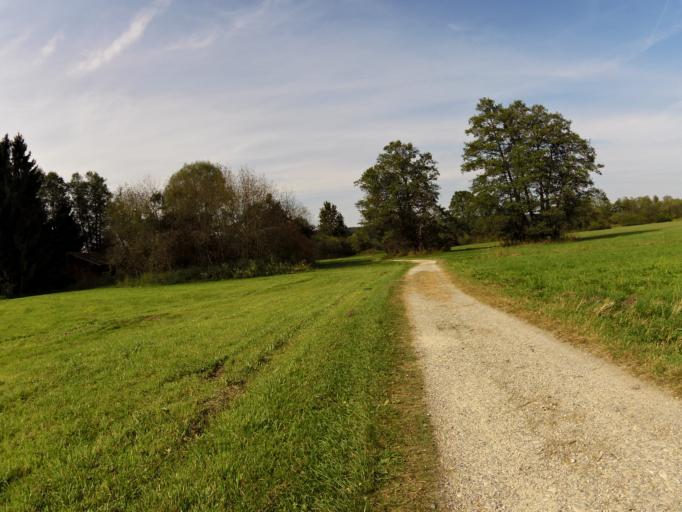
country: DE
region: Bavaria
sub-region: Upper Bavaria
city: Bernried
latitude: 47.8828
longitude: 11.2733
